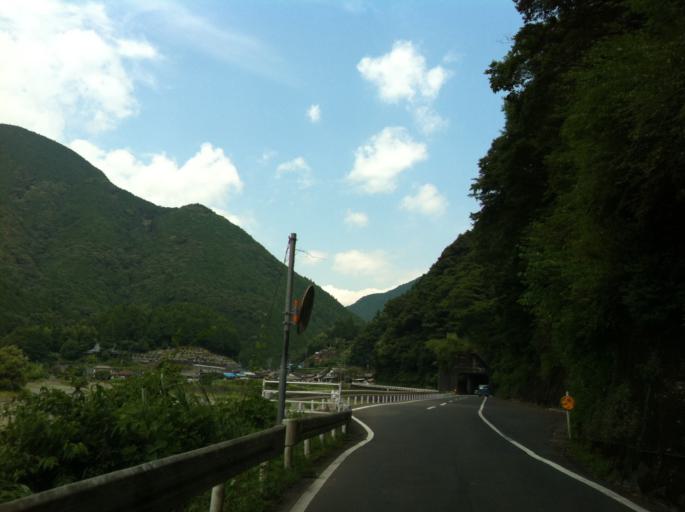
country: JP
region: Shizuoka
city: Shizuoka-shi
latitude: 35.1858
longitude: 138.3614
